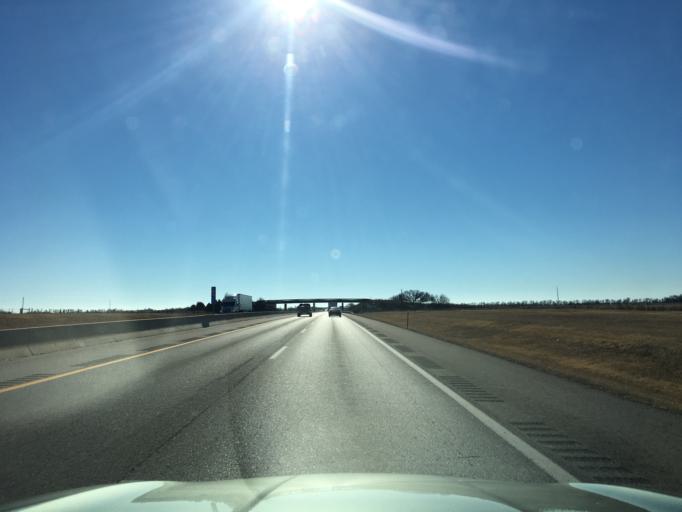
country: US
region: Kansas
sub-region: Sumner County
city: Wellington
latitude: 37.0456
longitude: -97.3383
